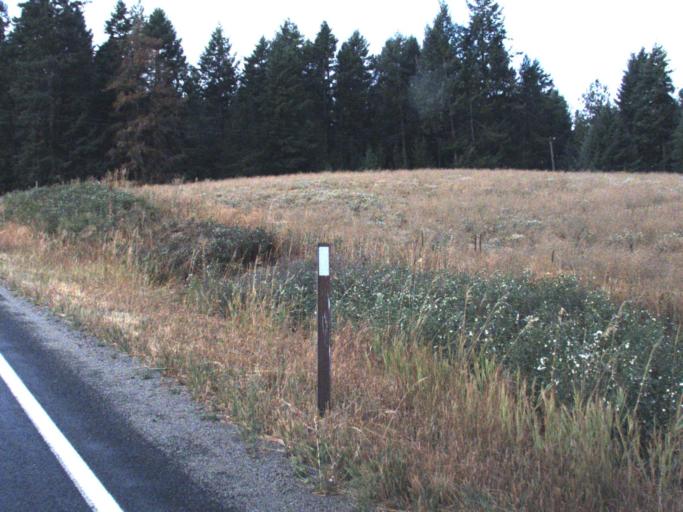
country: US
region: Washington
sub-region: Stevens County
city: Chewelah
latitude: 48.1177
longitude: -117.7546
